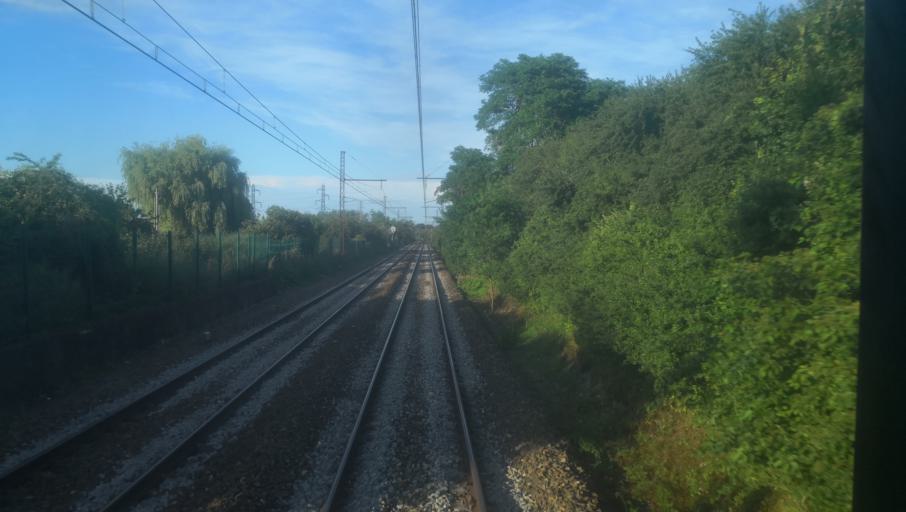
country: FR
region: Centre
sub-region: Departement de l'Indre
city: Deols
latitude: 46.8239
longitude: 1.7346
